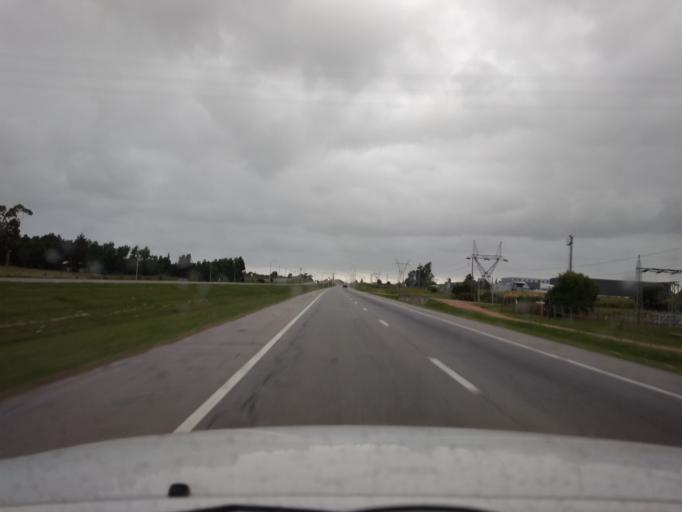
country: UY
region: Canelones
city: Las Piedras
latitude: -34.7125
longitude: -56.2433
